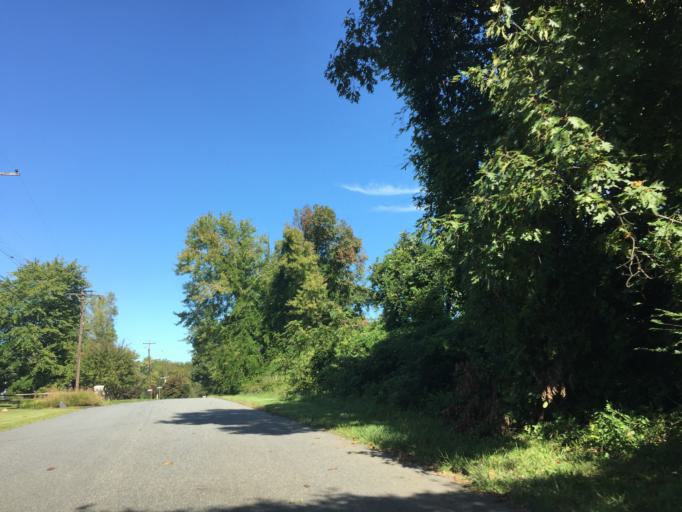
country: US
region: Maryland
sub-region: Baltimore County
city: White Marsh
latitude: 39.4127
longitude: -76.4123
